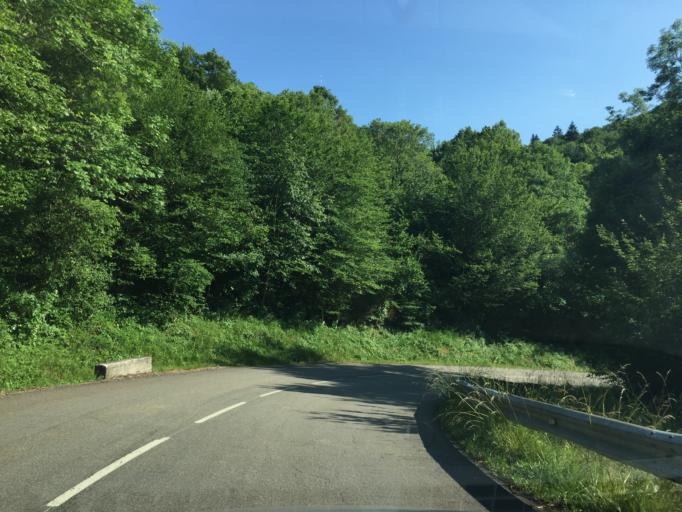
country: FR
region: Rhone-Alpes
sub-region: Departement de la Drome
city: Saint-Laurent-en-Royans
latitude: 45.0329
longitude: 5.3480
